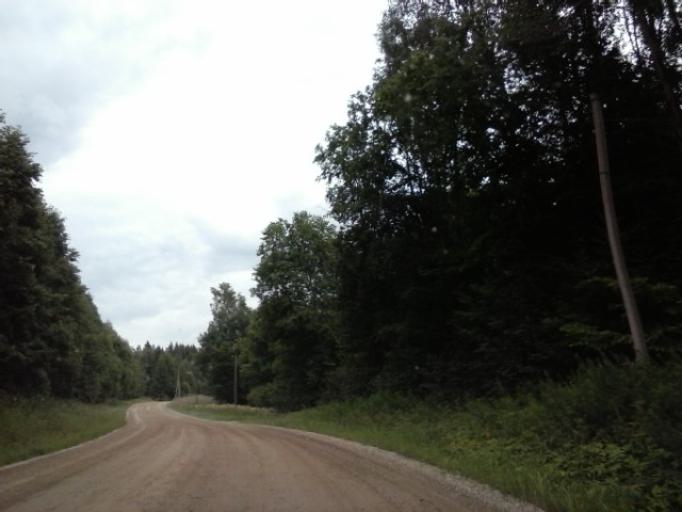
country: EE
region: Vorumaa
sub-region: Voru linn
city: Voru
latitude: 57.7477
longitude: 27.0700
